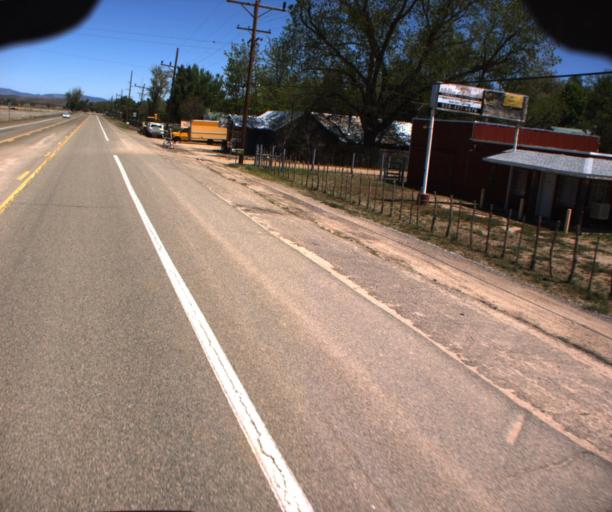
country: US
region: Arizona
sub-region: Yavapai County
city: Congress
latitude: 34.2684
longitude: -112.7272
